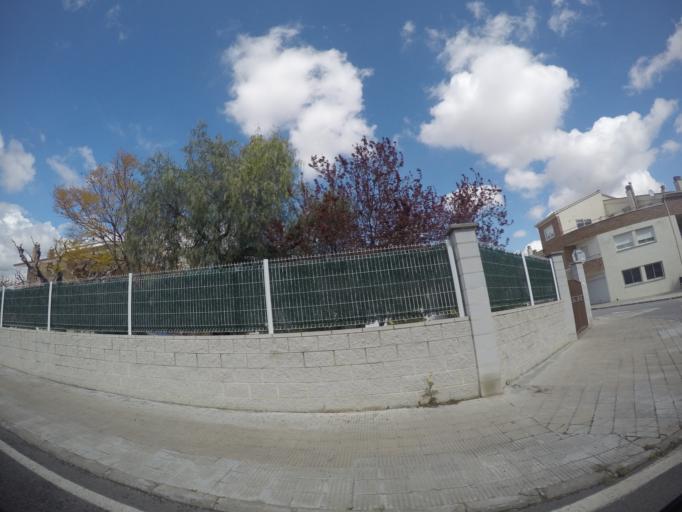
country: ES
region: Catalonia
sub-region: Provincia de Tarragona
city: Sant Jaume dels Domenys
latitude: 41.2813
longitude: 1.5479
